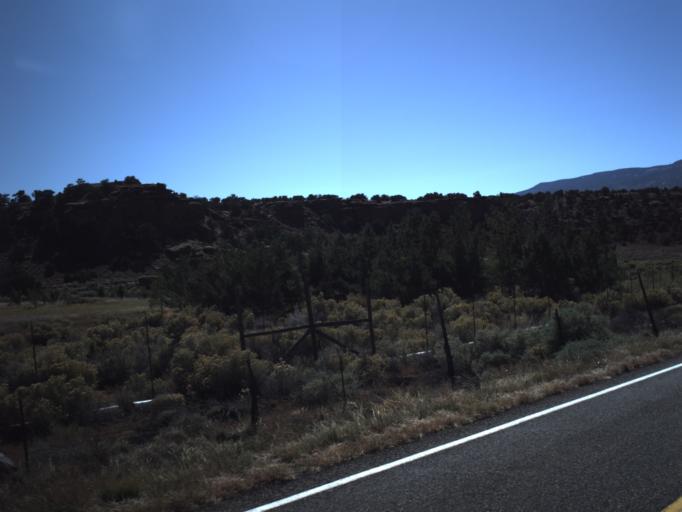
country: US
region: Utah
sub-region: Wayne County
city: Loa
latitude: 38.2888
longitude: -111.3950
